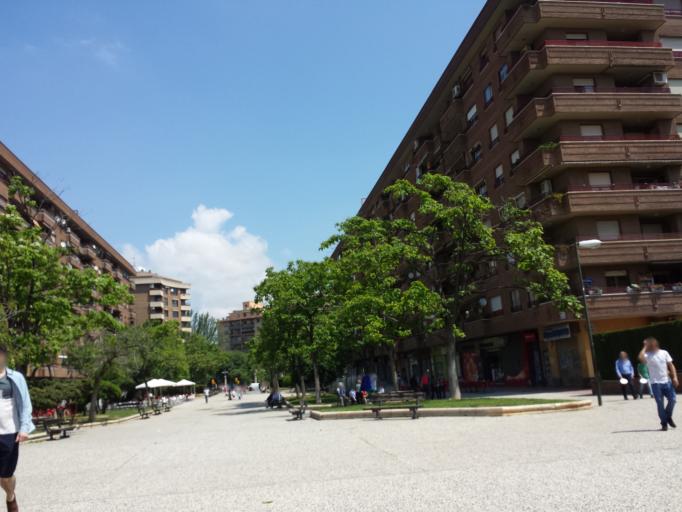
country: ES
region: Aragon
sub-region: Provincia de Zaragoza
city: Almozara
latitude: 41.6586
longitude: -0.8959
